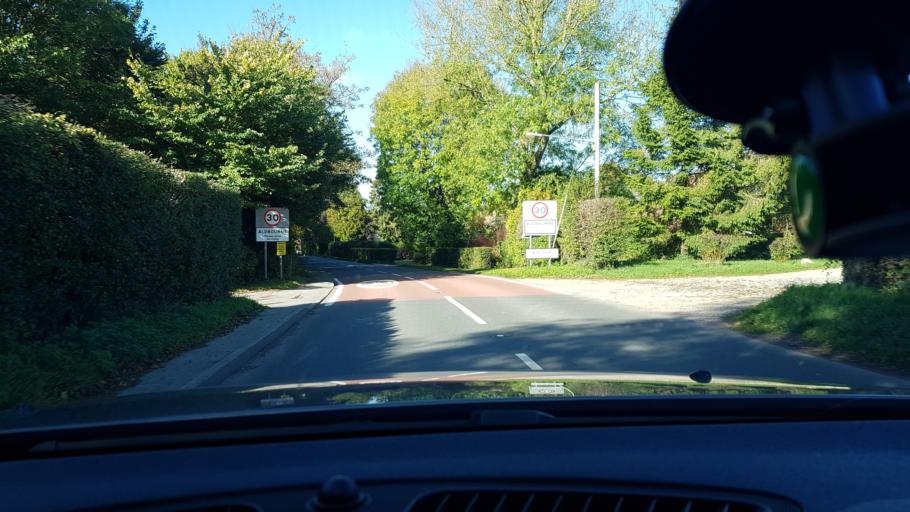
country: GB
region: England
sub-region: Wiltshire
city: Aldbourne
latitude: 51.4754
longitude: -1.6149
